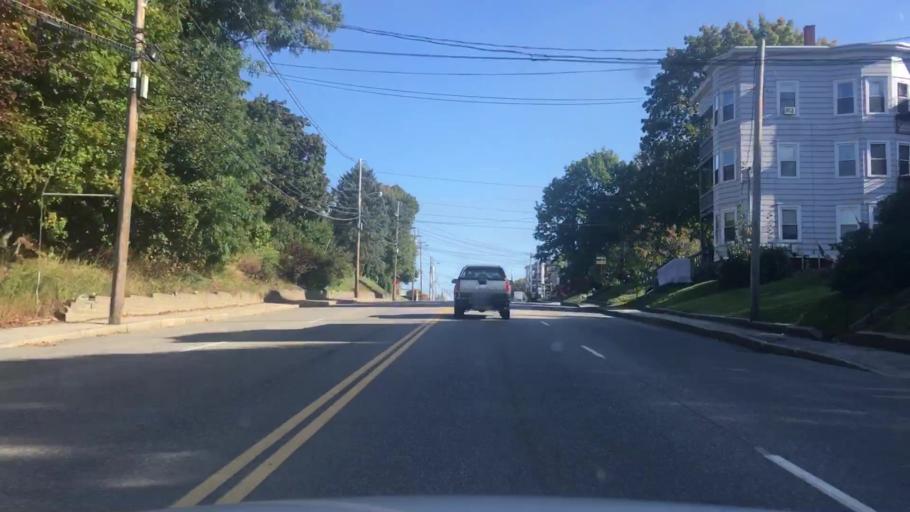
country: US
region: Maine
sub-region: Androscoggin County
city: Lewiston
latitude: 44.0868
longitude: -70.2083
